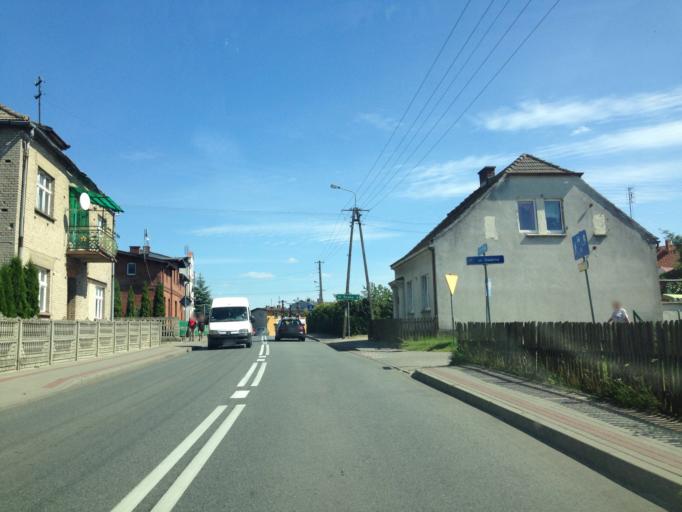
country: PL
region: Kujawsko-Pomorskie
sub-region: Powiat swiecki
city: Osie
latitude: 53.6001
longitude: 18.3418
